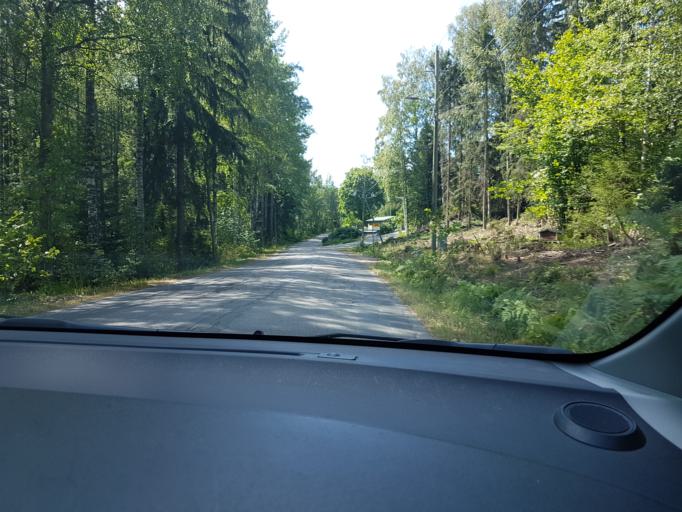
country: FI
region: Uusimaa
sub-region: Helsinki
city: Kilo
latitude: 60.3345
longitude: 24.7841
